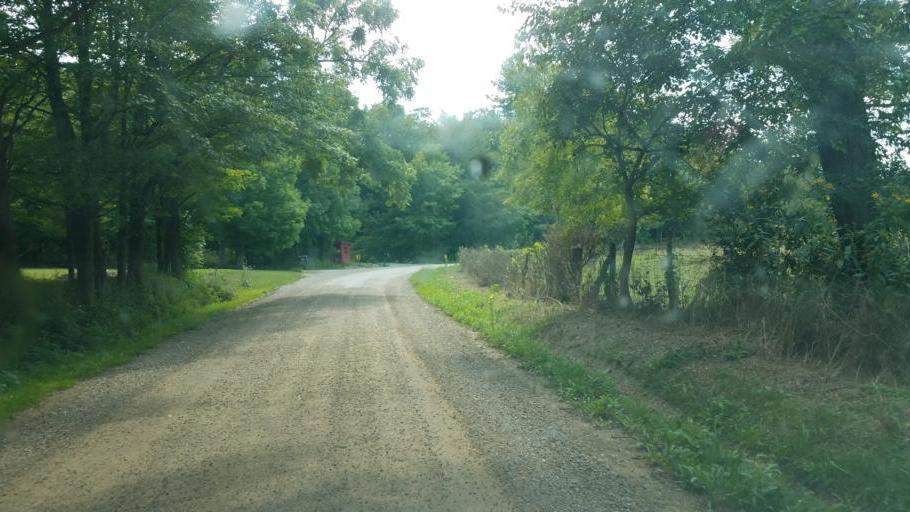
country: US
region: Ohio
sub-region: Knox County
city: Mount Vernon
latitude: 40.3391
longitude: -82.5718
